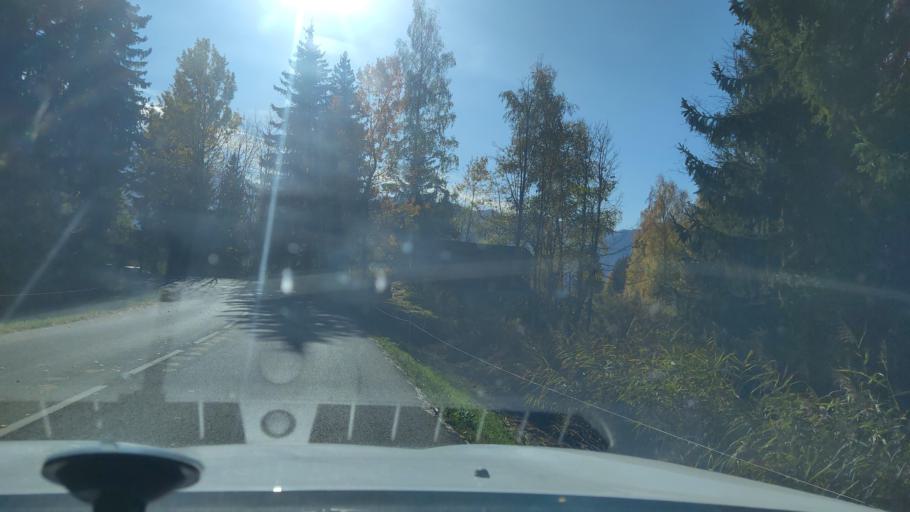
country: FR
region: Rhone-Alpes
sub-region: Departement de la Savoie
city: Beaufort
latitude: 45.7431
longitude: 6.5634
